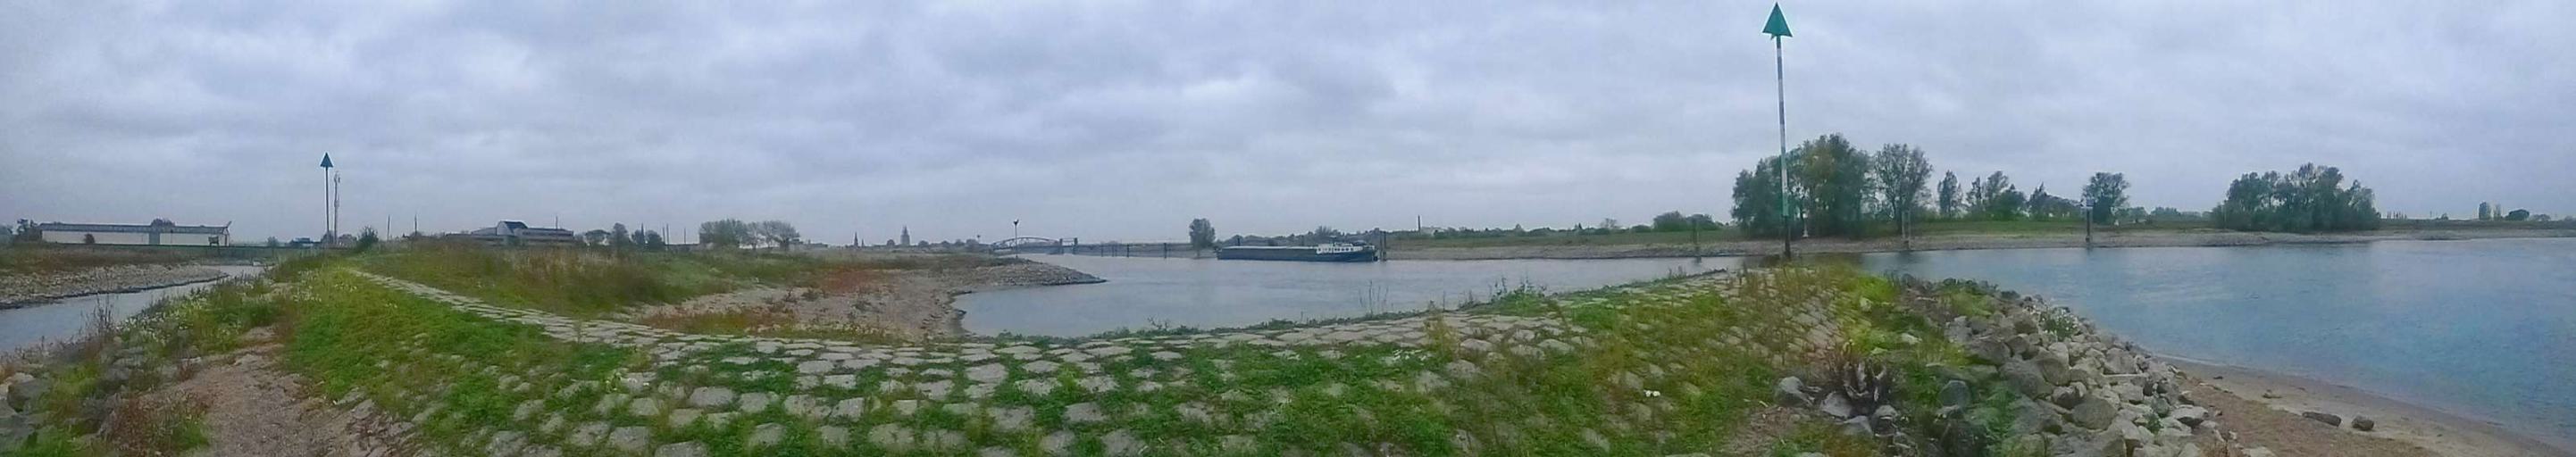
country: NL
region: Gelderland
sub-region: Gemeente Zutphen
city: Zutphen
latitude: 52.1497
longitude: 6.1846
